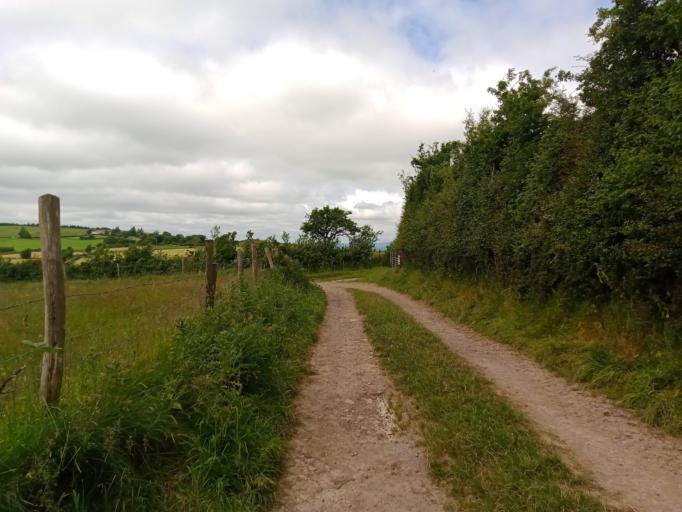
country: IE
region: Leinster
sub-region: Kilkenny
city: Ballyragget
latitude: 52.7942
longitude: -7.4580
